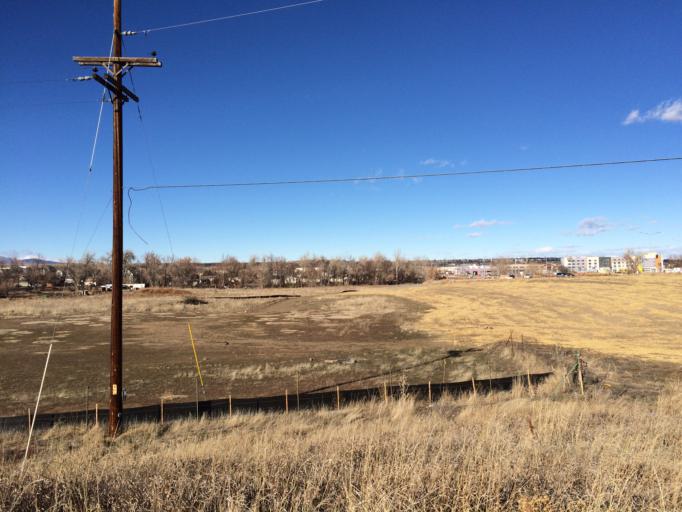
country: US
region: Colorado
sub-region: Boulder County
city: Superior
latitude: 39.9498
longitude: -105.1659
